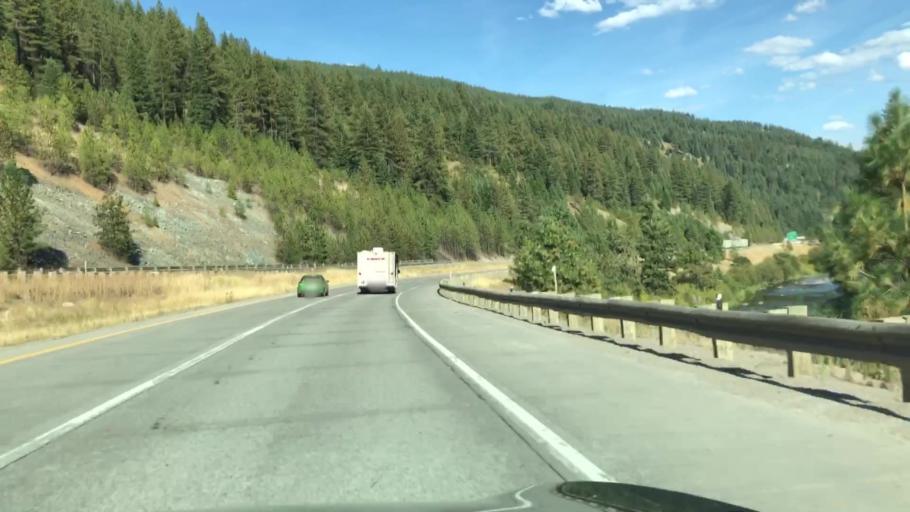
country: US
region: Montana
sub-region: Mineral County
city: Superior
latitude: 47.3022
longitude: -115.1940
